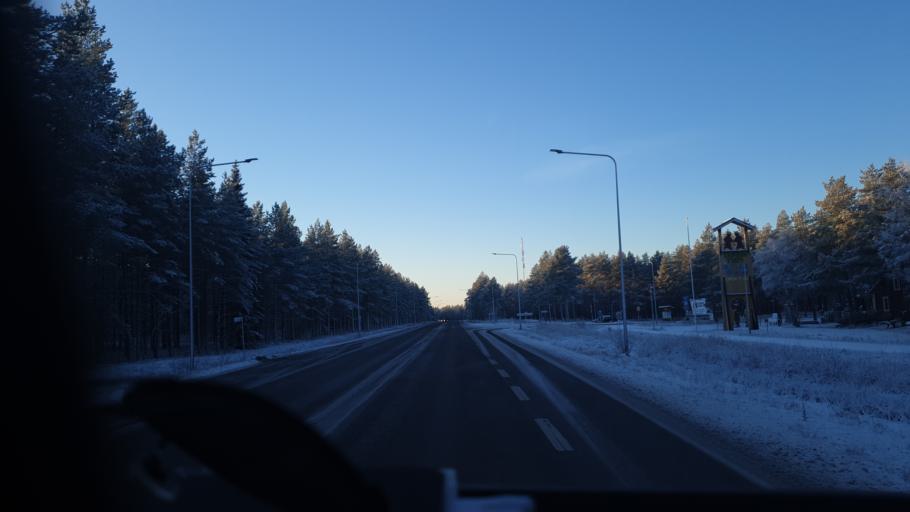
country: FI
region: Northern Ostrobothnia
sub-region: Ylivieska
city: Kalajoki
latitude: 64.2410
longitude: 23.8462
